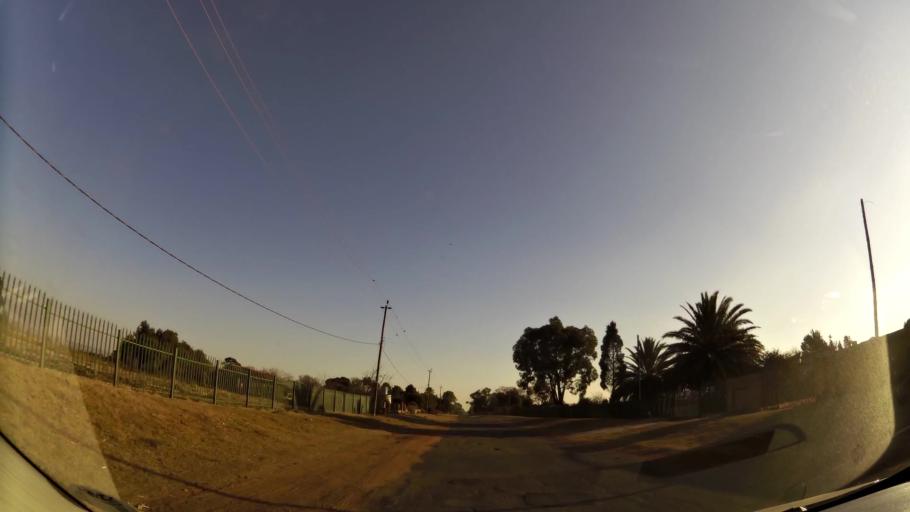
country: ZA
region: Gauteng
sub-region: West Rand District Municipality
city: Randfontein
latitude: -26.2138
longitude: 27.6566
